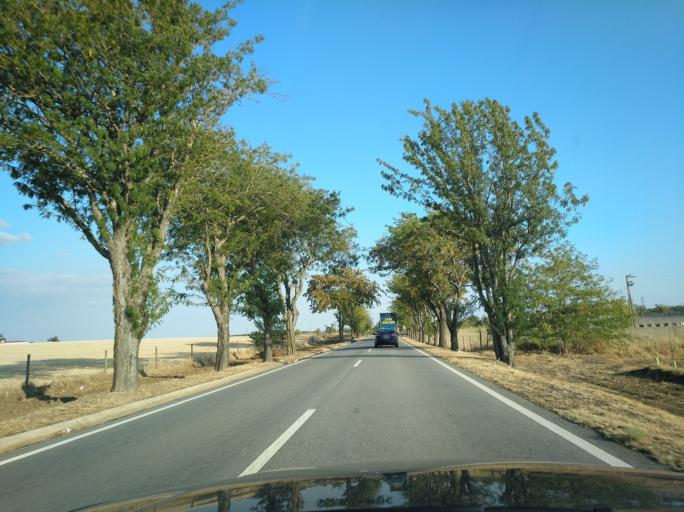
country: PT
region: Portalegre
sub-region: Campo Maior
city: Campo Maior
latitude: 39.0330
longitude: -7.0868
